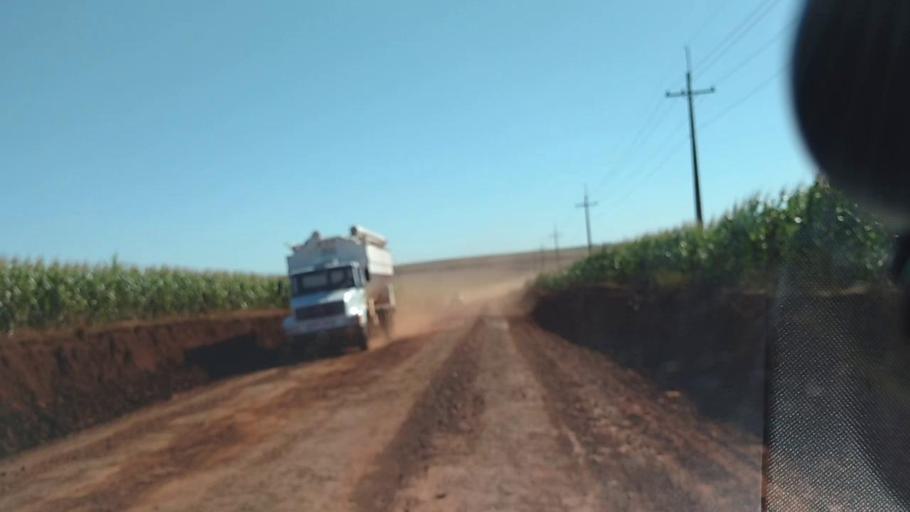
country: PY
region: Alto Parana
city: Naranjal
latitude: -25.9753
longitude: -55.2238
